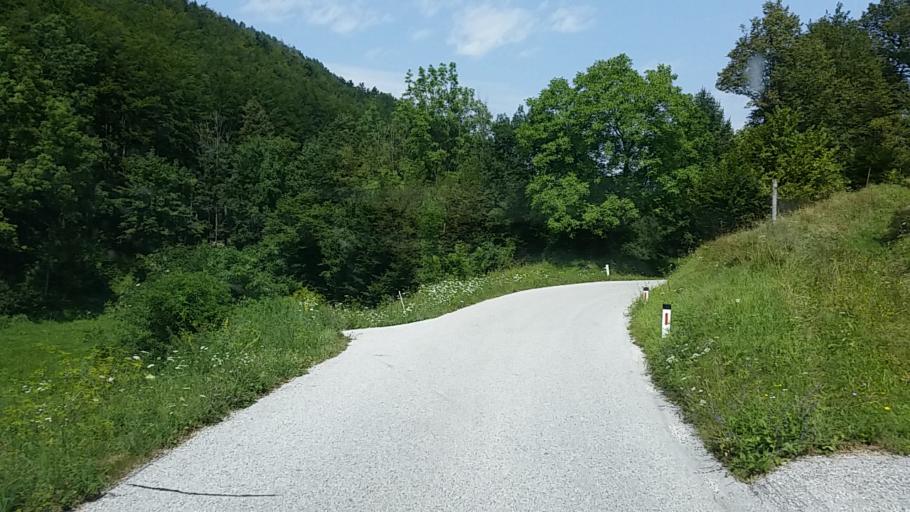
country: SI
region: Tolmin
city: Tolmin
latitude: 46.1039
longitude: 13.8023
